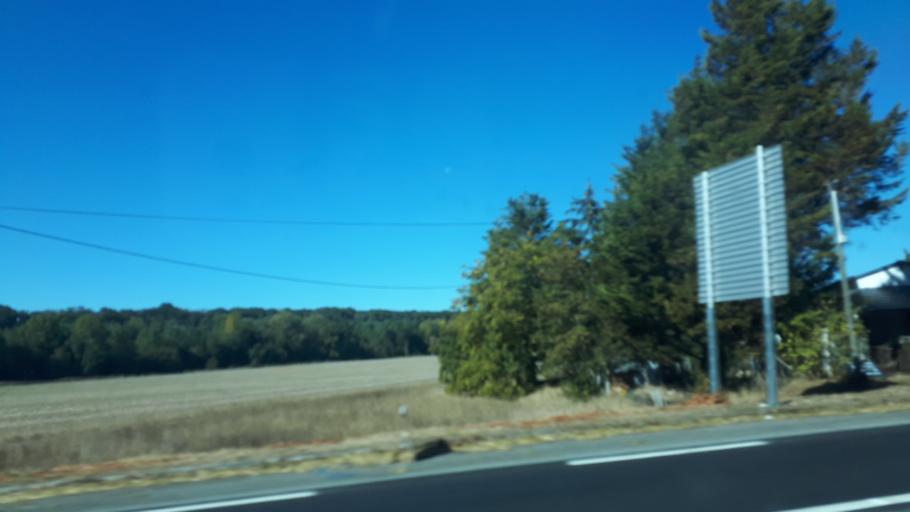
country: FR
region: Centre
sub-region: Departement d'Eure-et-Loir
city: Marboue
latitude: 48.0987
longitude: 1.3303
